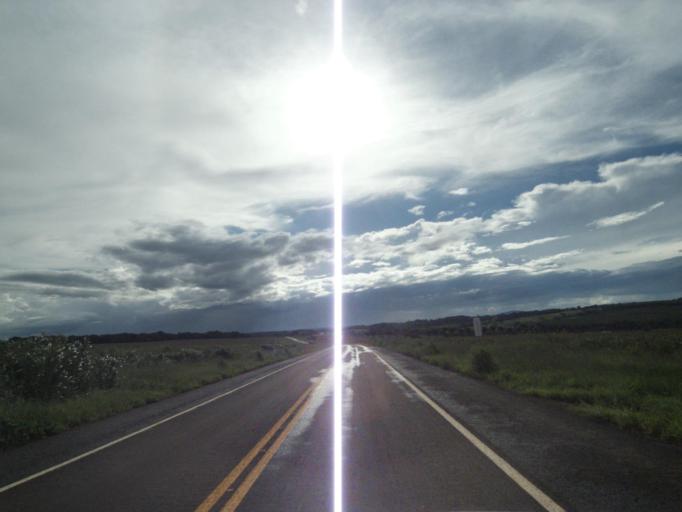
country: BR
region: Goias
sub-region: Jaragua
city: Jaragua
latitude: -15.9020
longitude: -49.5359
